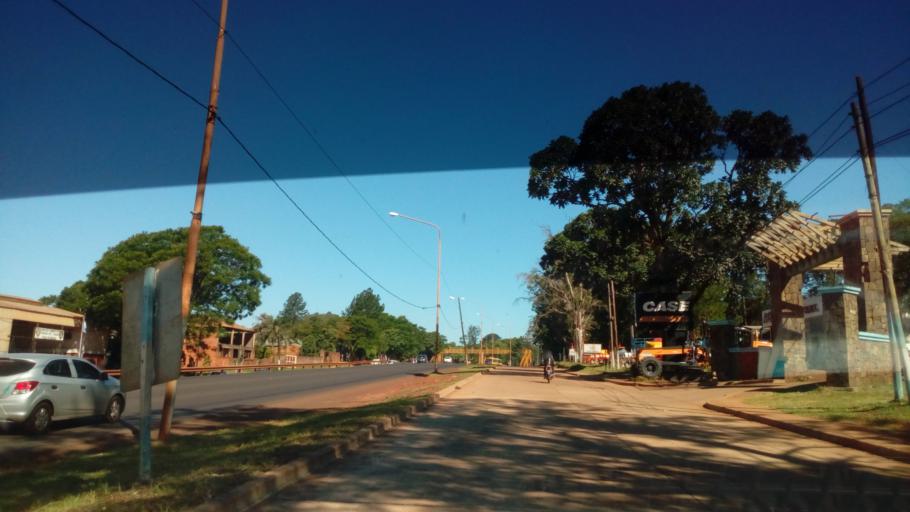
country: AR
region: Misiones
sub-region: Departamento de Capital
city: Posadas
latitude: -27.4275
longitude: -55.8936
